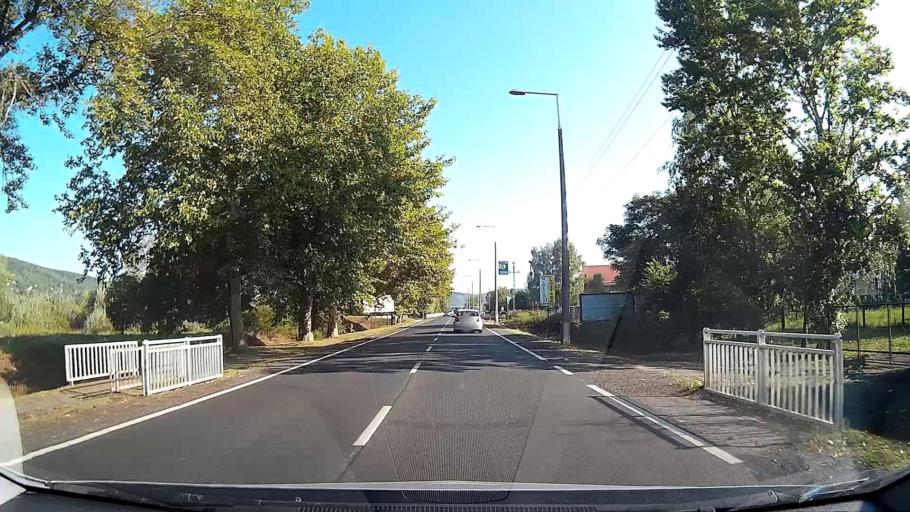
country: HU
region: Pest
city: Visegrad
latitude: 47.7811
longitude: 18.9672
